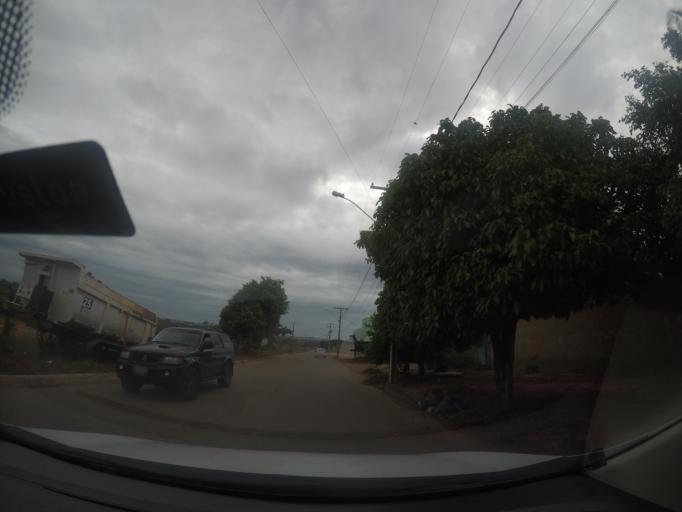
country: BR
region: Goias
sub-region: Goiania
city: Goiania
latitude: -16.6439
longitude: -49.3372
